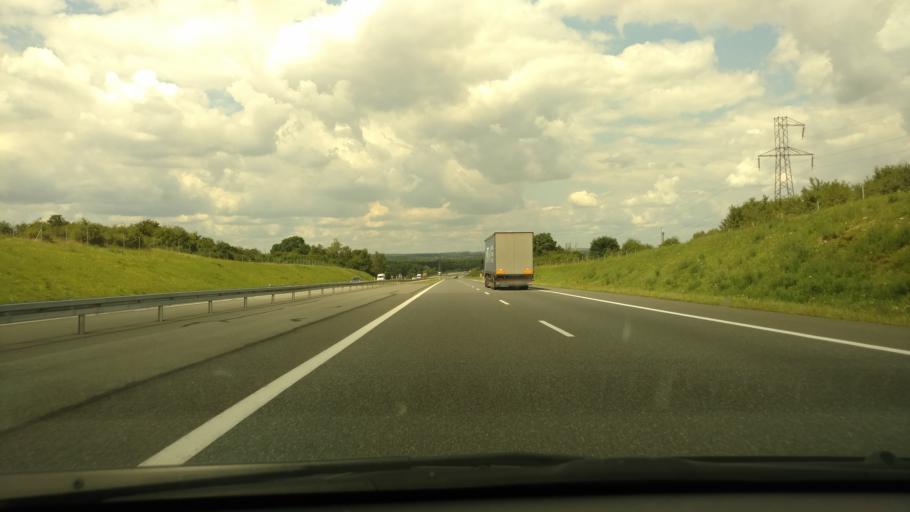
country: PL
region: Silesian Voivodeship
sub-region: Powiat bierunsko-ledzinski
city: Imielin
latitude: 50.1750
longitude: 19.2058
